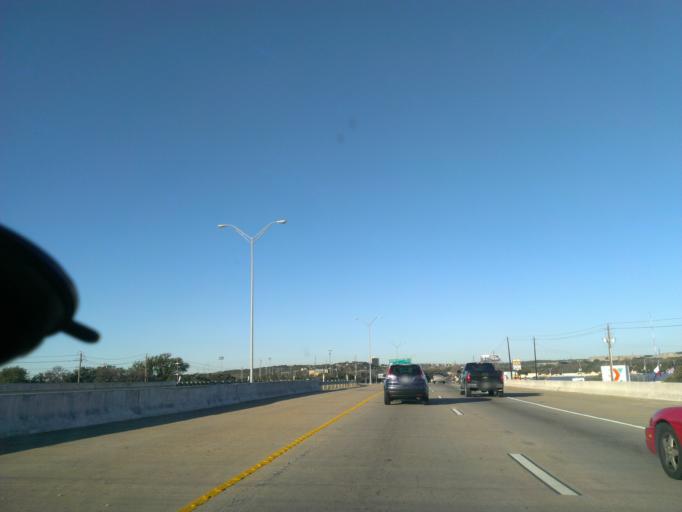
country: US
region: Texas
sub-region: Travis County
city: Barton Creek
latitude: 30.2355
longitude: -97.8519
